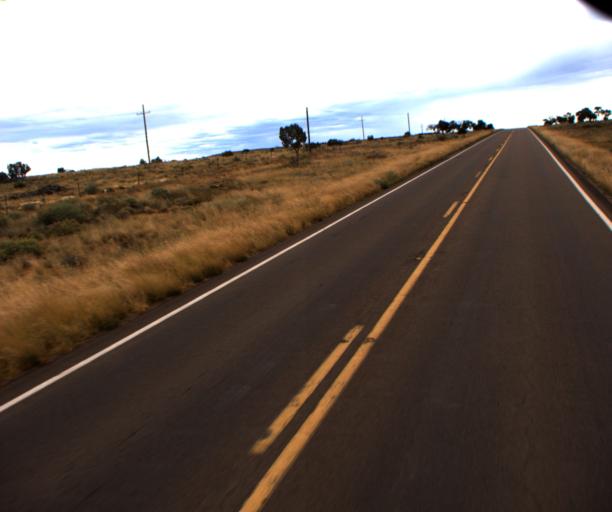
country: US
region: Arizona
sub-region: Navajo County
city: Snowflake
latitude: 34.5545
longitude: -110.0807
